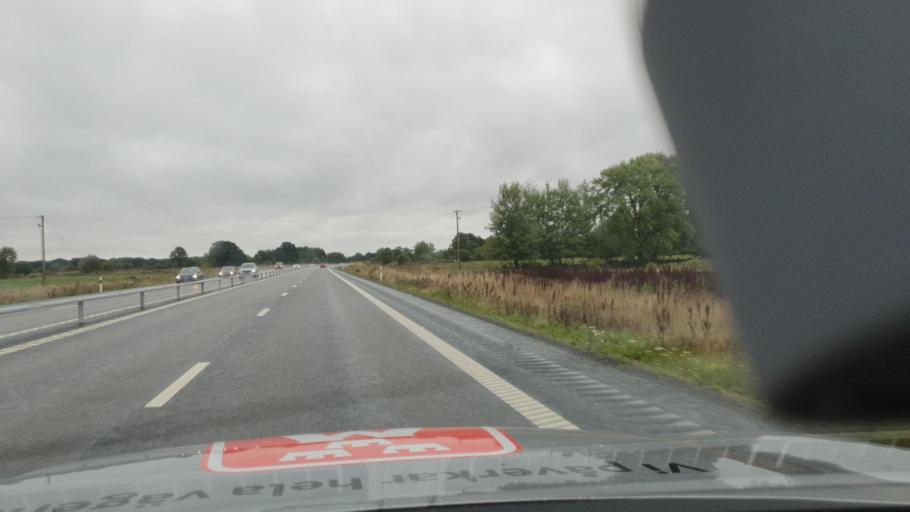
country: SE
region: Skane
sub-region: Kristianstads Kommun
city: Onnestad
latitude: 55.9668
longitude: 14.0239
